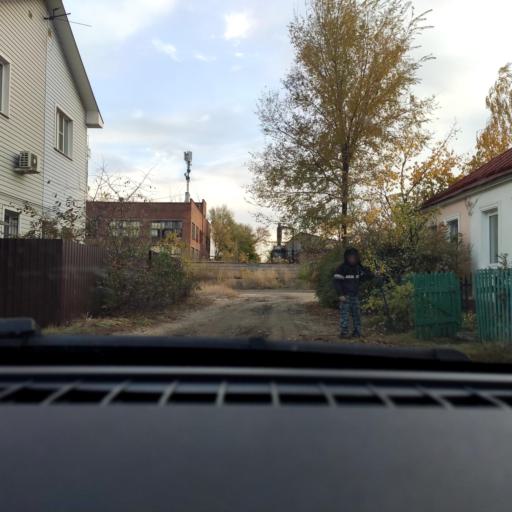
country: RU
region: Voronezj
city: Maslovka
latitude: 51.6067
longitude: 39.2330
